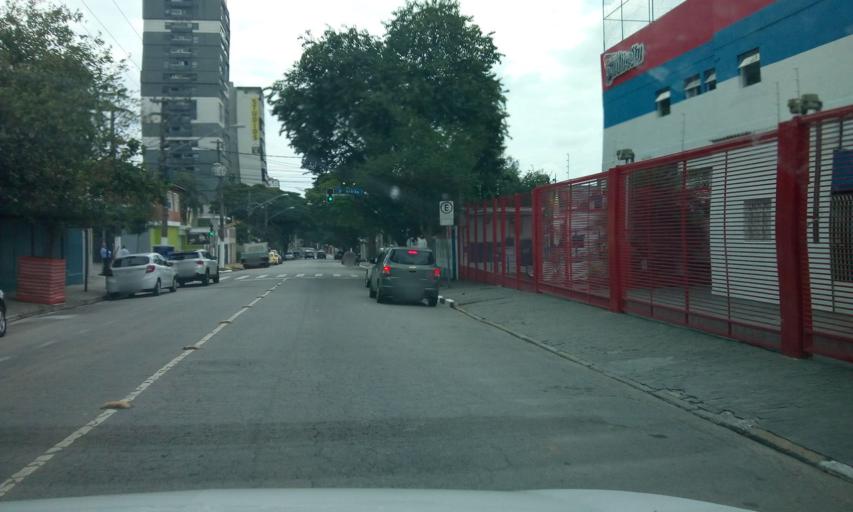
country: BR
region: Sao Paulo
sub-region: Diadema
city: Diadema
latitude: -23.6253
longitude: -46.6648
